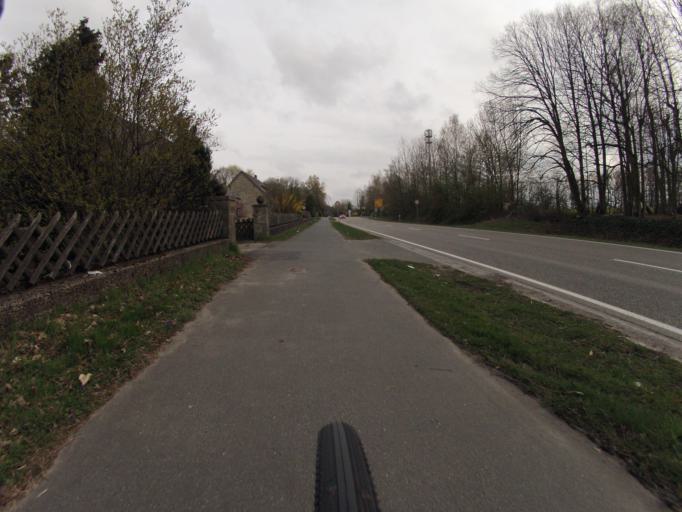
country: DE
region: North Rhine-Westphalia
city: Ibbenburen
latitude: 52.2978
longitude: 7.6952
